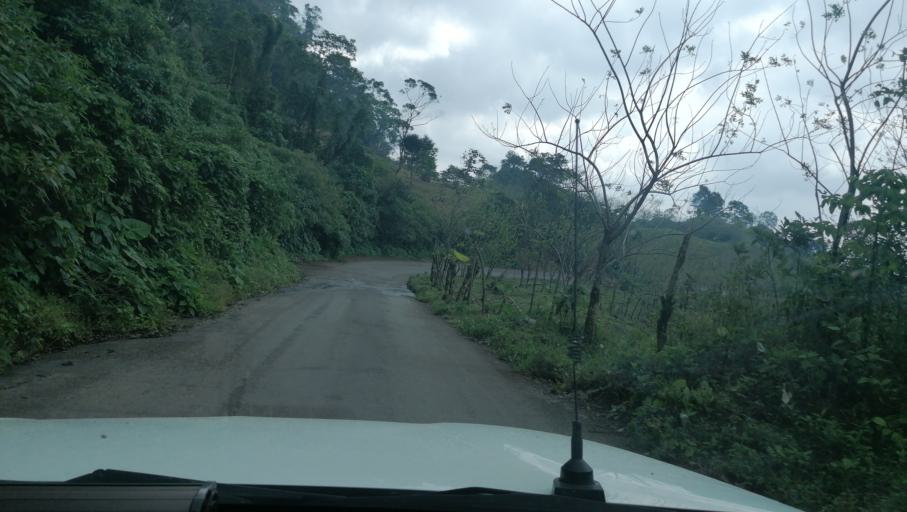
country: MX
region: Chiapas
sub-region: Francisco Leon
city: San Miguel la Sardina
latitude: 17.2426
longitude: -93.2937
